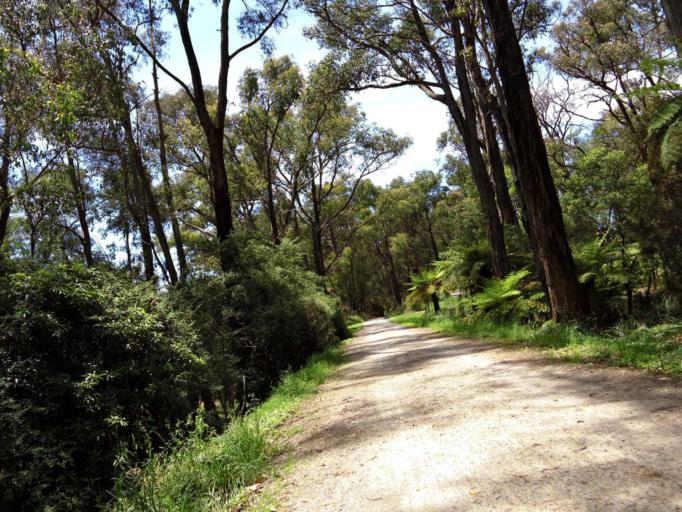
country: AU
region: Victoria
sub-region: Yarra Ranges
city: Mount Evelyn
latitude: -37.7822
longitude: 145.3988
